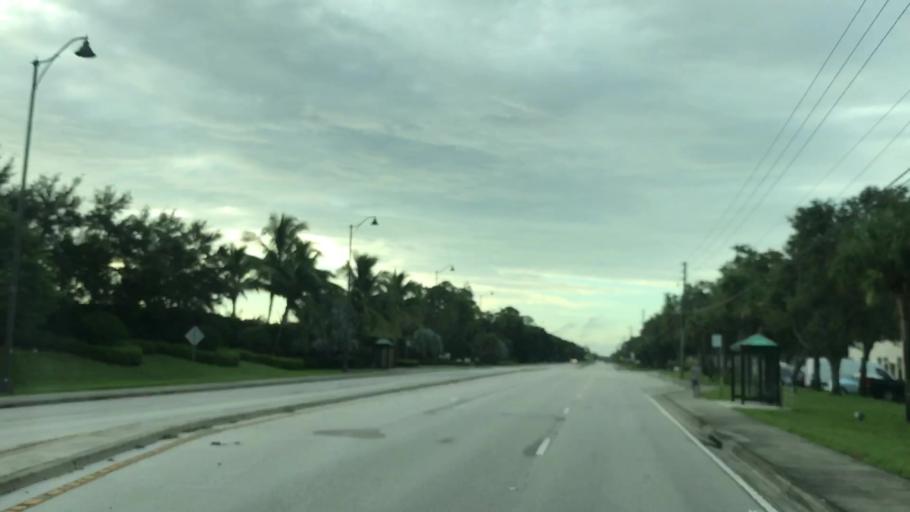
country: US
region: Florida
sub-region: Lee County
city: Bonita Springs
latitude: 26.3690
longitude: -81.7985
